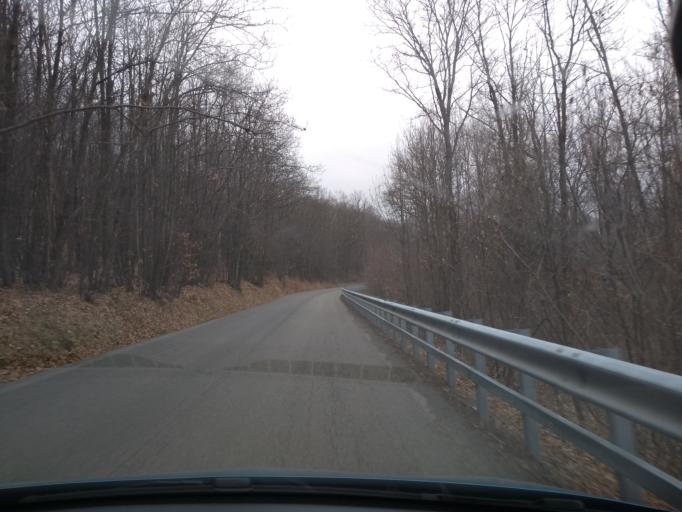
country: IT
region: Piedmont
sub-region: Provincia di Torino
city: Palazzo Canavese
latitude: 45.4798
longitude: 7.9748
